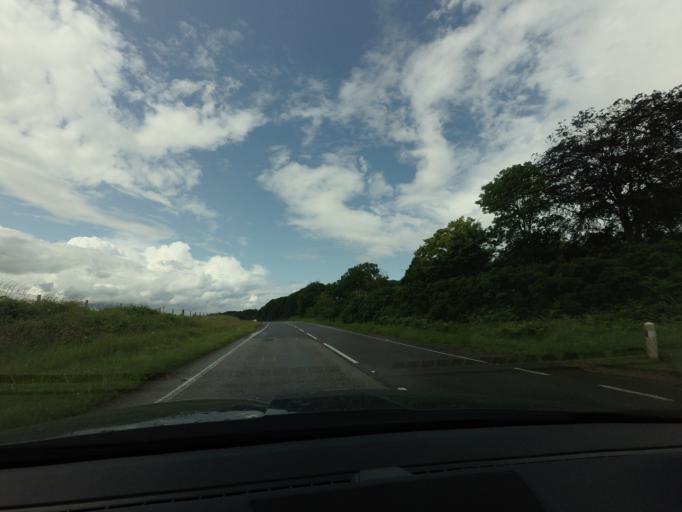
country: GB
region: Scotland
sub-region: Moray
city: Lhanbryd
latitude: 57.6298
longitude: -3.1724
